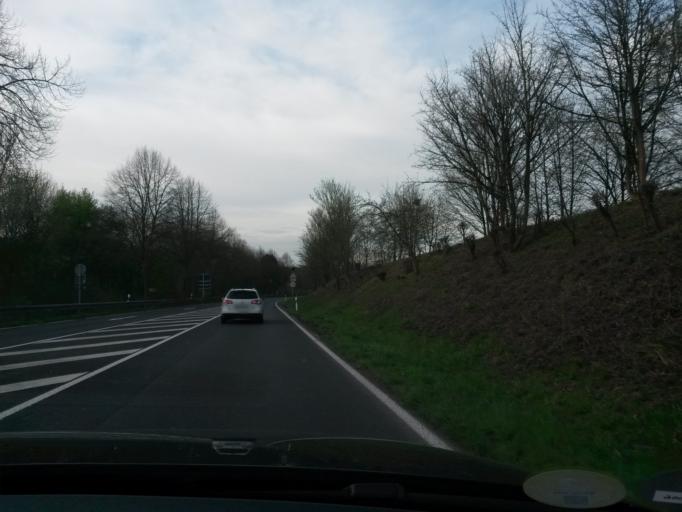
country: DE
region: North Rhine-Westphalia
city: Lohmar
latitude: 50.8852
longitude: 7.2481
